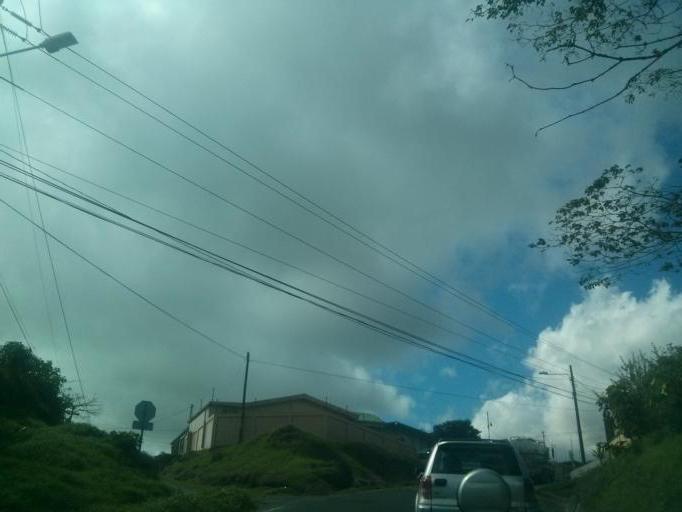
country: CR
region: Cartago
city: Cot
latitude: 9.8880
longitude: -83.8524
